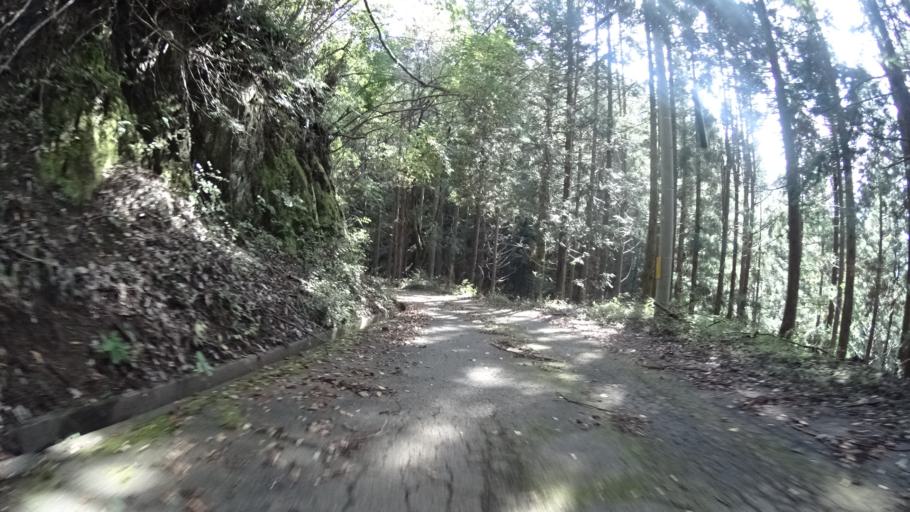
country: JP
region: Yamanashi
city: Otsuki
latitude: 35.5756
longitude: 138.9877
